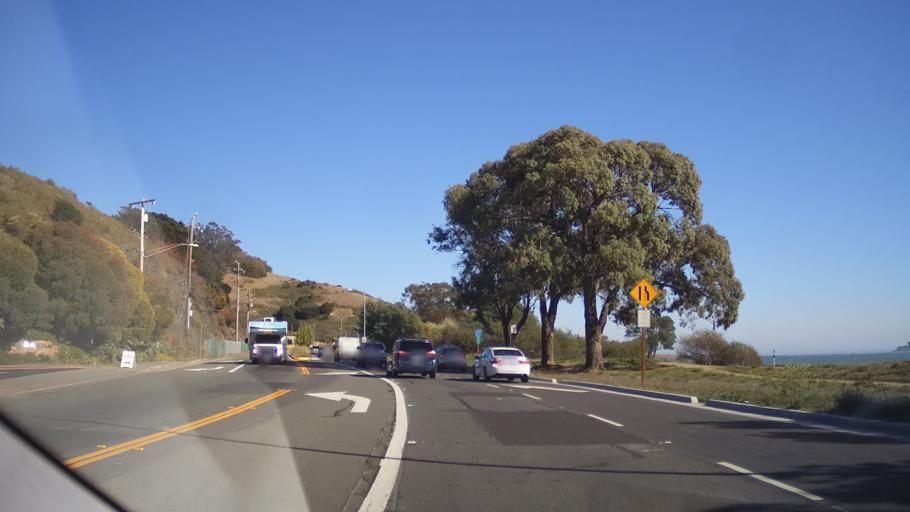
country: US
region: California
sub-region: Marin County
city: Corte Madera
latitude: 37.9444
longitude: -122.5060
